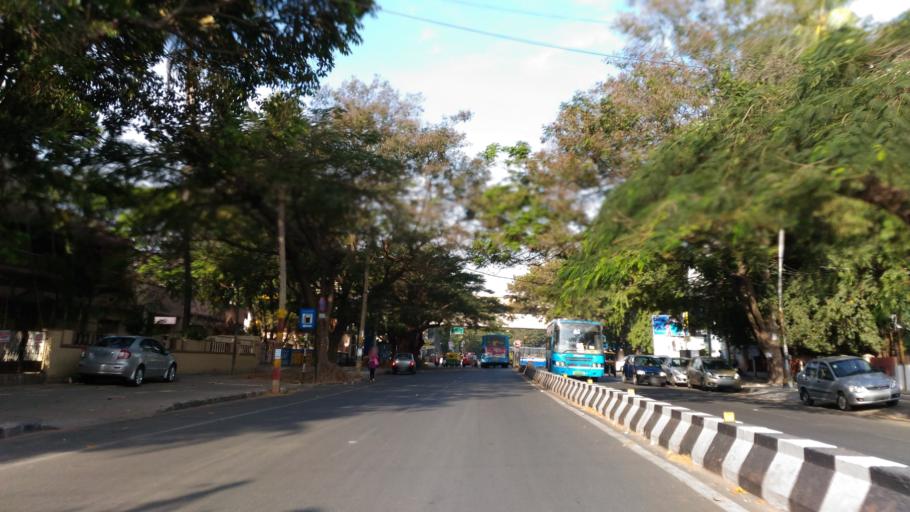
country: IN
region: Karnataka
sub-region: Bangalore Urban
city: Bangalore
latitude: 12.9367
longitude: 77.5813
